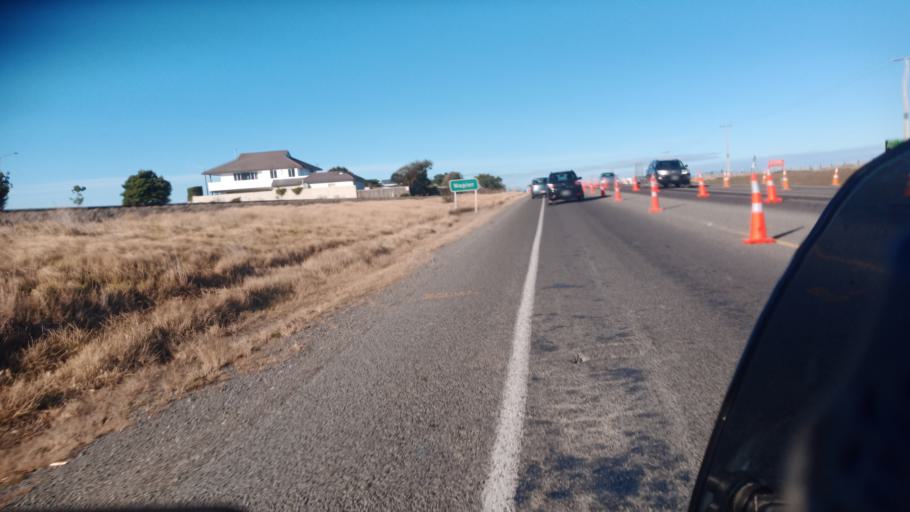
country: NZ
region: Hawke's Bay
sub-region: Napier City
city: Napier
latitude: -39.4576
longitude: 176.8723
